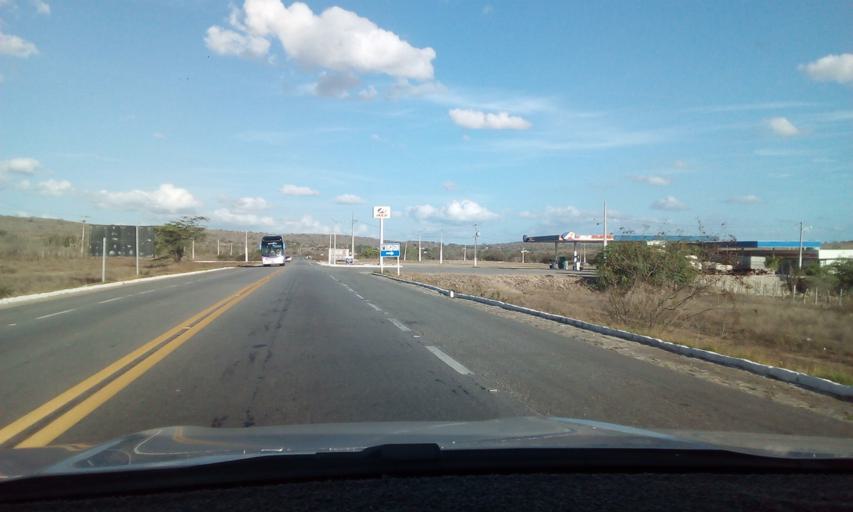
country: BR
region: Paraiba
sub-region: Pocinhos
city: Pocinhos
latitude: -7.1529
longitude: -36.1034
